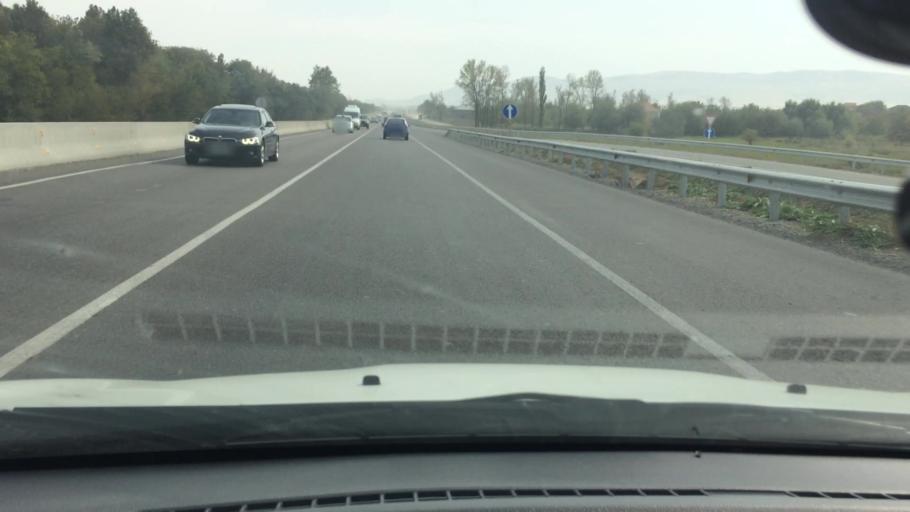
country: GE
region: Kvemo Kartli
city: Rust'avi
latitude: 41.6276
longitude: 44.9227
